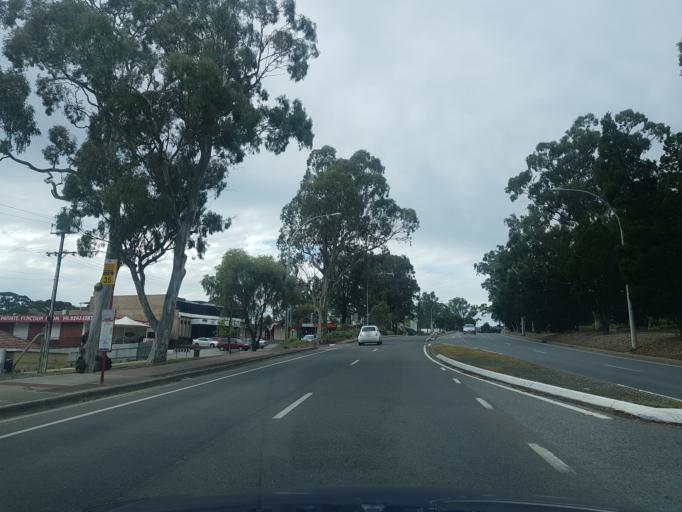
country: AU
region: South Australia
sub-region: Campbelltown
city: Athelstone
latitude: -34.8539
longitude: 138.6976
